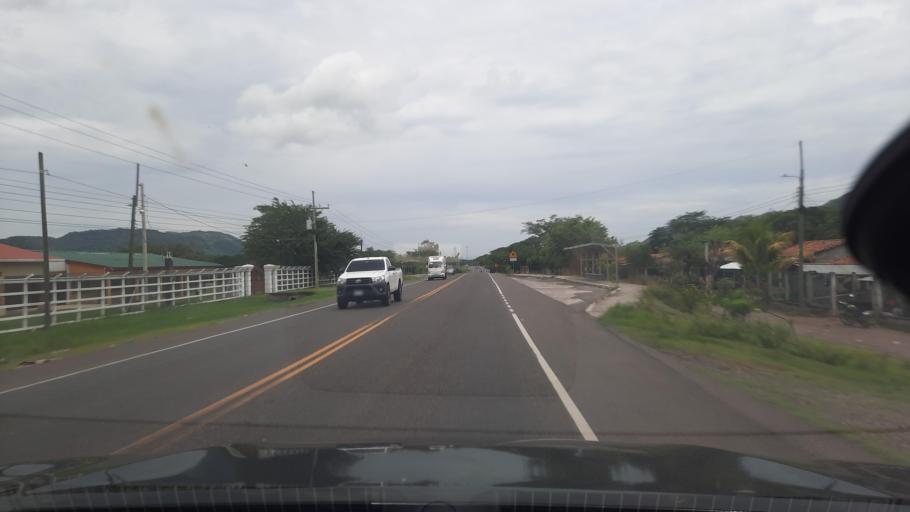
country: HN
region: Valle
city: Jicaro Galan
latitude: 13.5113
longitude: -87.4401
